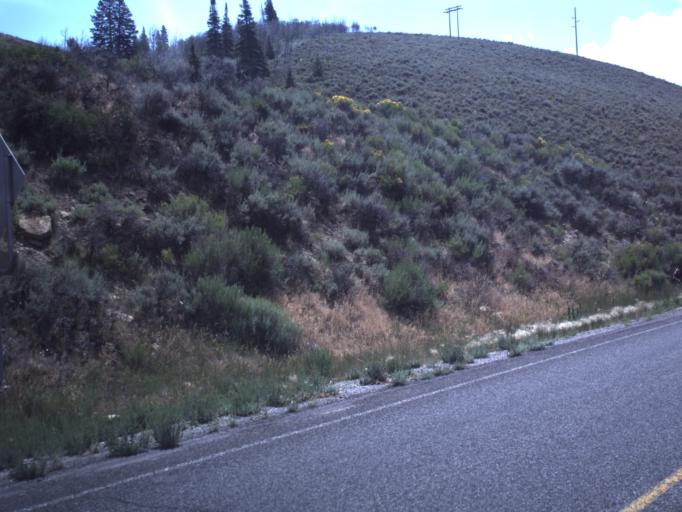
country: US
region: Utah
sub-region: Carbon County
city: Helper
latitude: 39.7679
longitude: -111.1405
